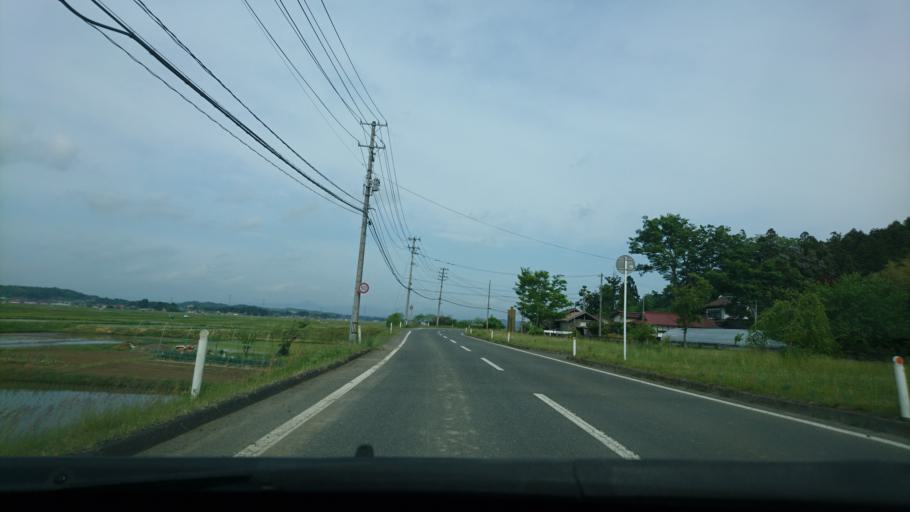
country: JP
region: Iwate
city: Ichinoseki
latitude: 38.8081
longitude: 141.0673
